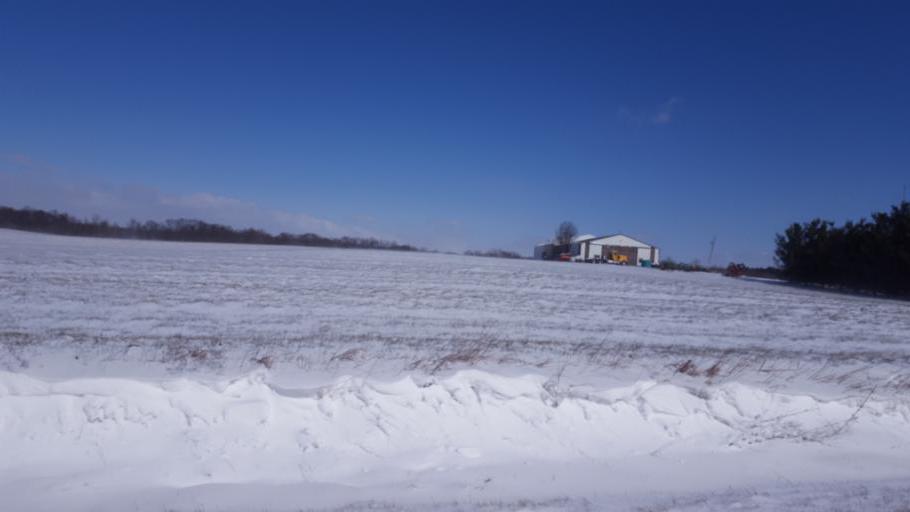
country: US
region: Ohio
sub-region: Morrow County
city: Mount Gilead
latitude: 40.4805
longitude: -82.7019
